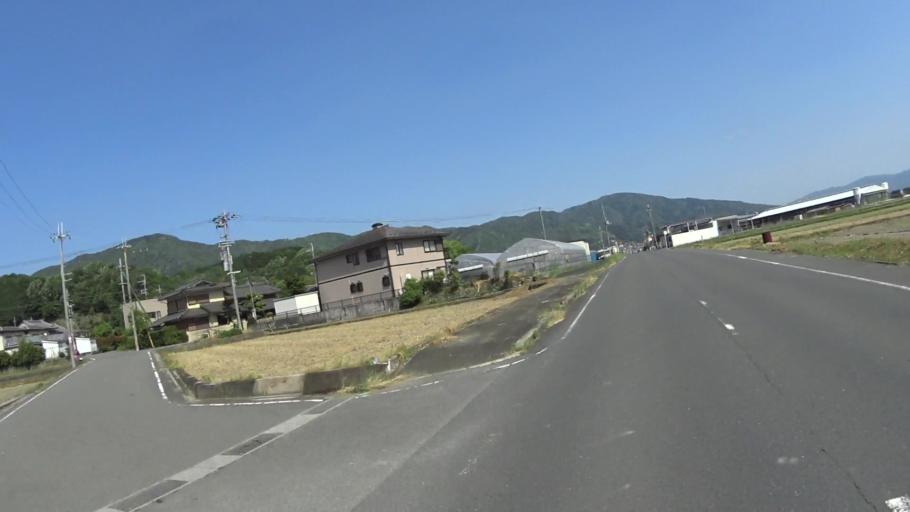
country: JP
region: Kyoto
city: Kameoka
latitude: 35.0677
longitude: 135.5547
